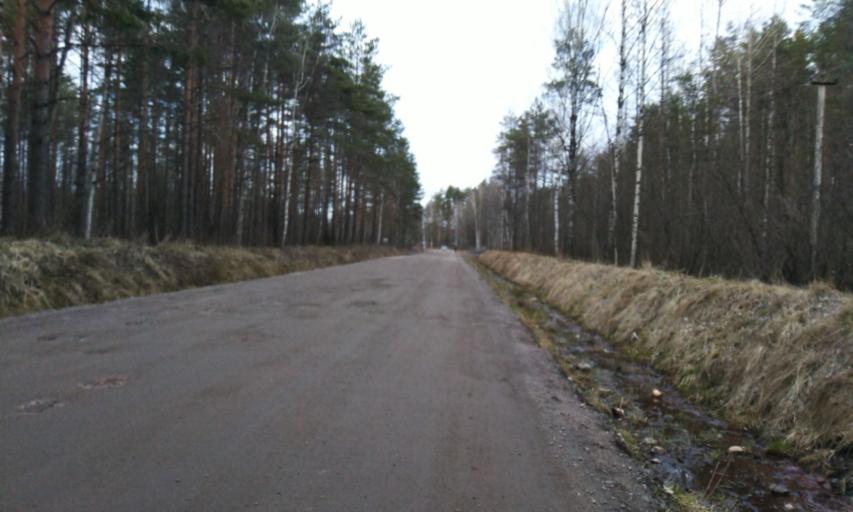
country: RU
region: Leningrad
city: Toksovo
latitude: 60.1174
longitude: 30.4823
